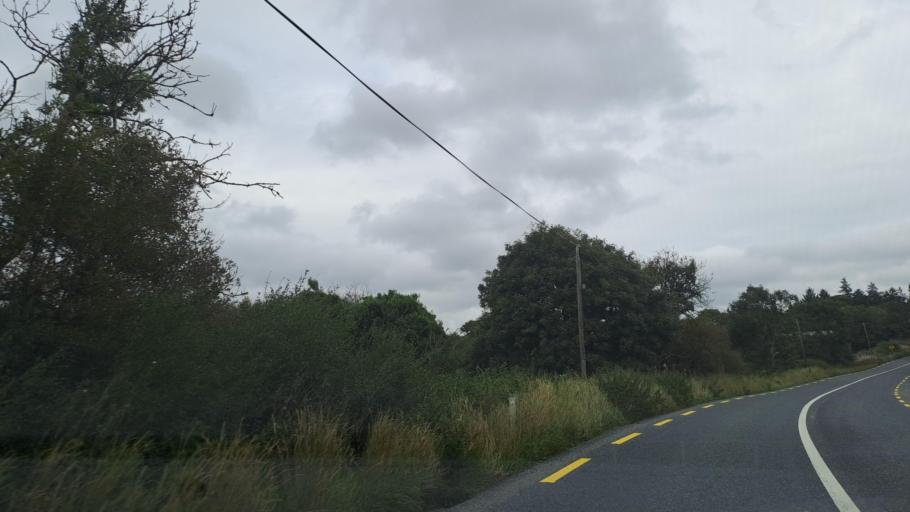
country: IE
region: Ulster
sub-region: An Cabhan
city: Bailieborough
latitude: 53.9566
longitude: -6.9430
